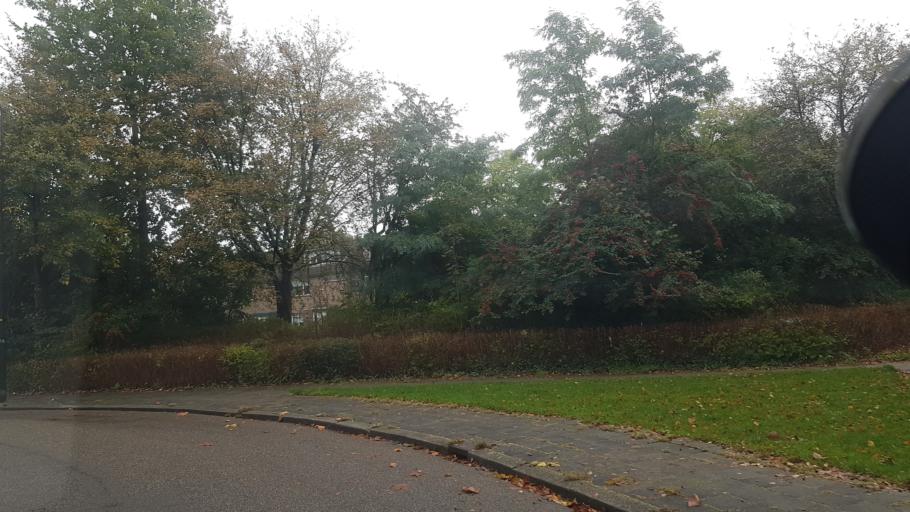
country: NL
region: Gelderland
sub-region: Gemeente Apeldoorn
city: Apeldoorn
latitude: 52.2209
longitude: 5.9932
